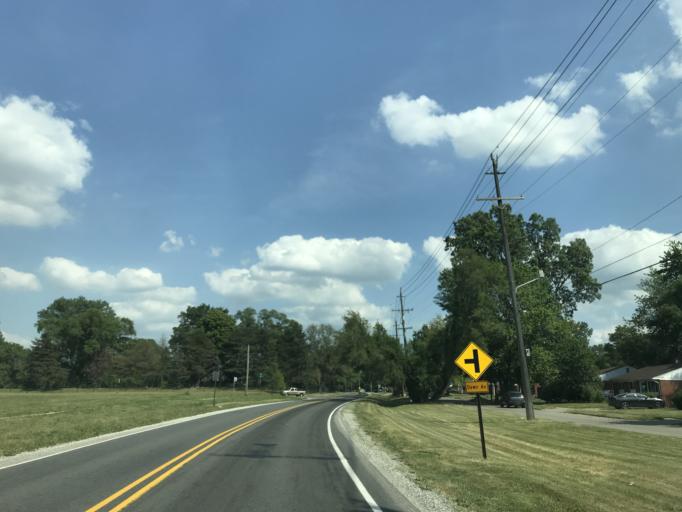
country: US
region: Michigan
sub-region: Washtenaw County
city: Ypsilanti
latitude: 42.2600
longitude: -83.5844
